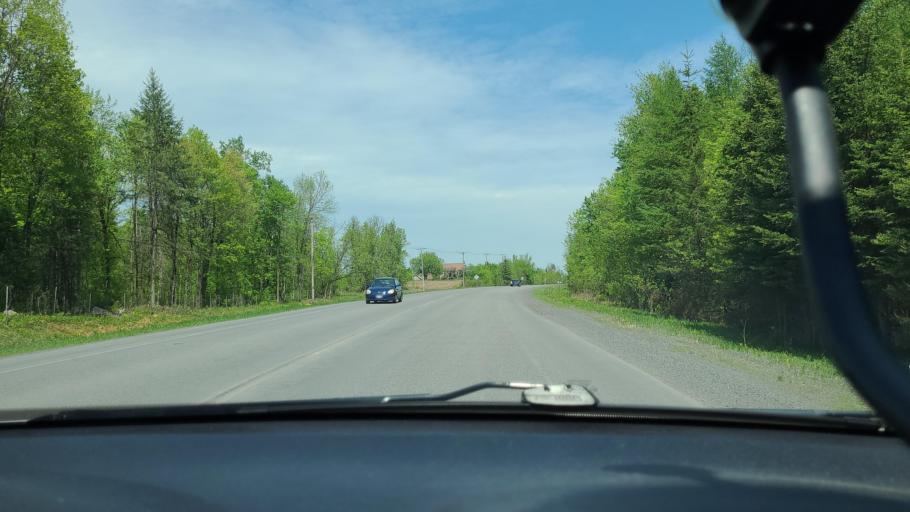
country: CA
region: Quebec
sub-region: Laurentides
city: Saint-Colomban
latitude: 45.6770
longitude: -74.1964
